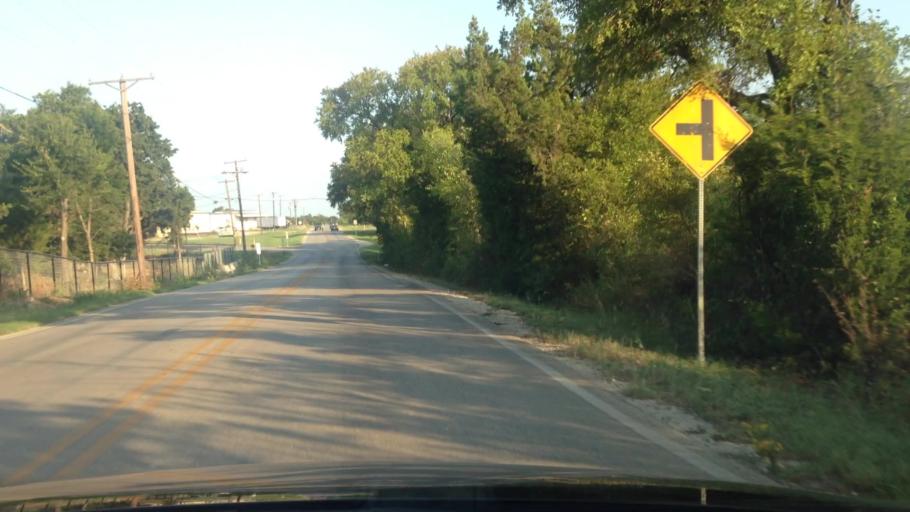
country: US
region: Texas
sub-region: Tarrant County
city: Rendon
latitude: 32.5960
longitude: -97.2581
